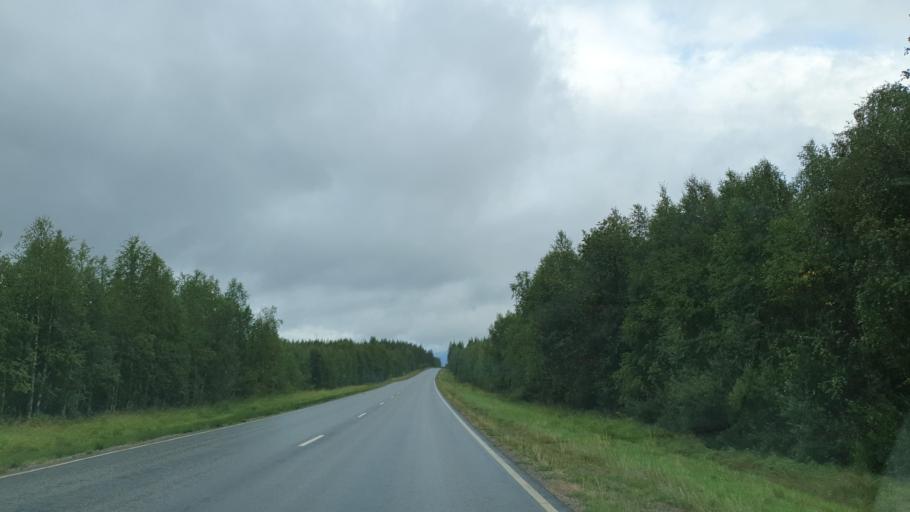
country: FI
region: Lapland
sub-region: Tunturi-Lappi
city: Kolari
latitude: 67.3947
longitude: 23.8065
